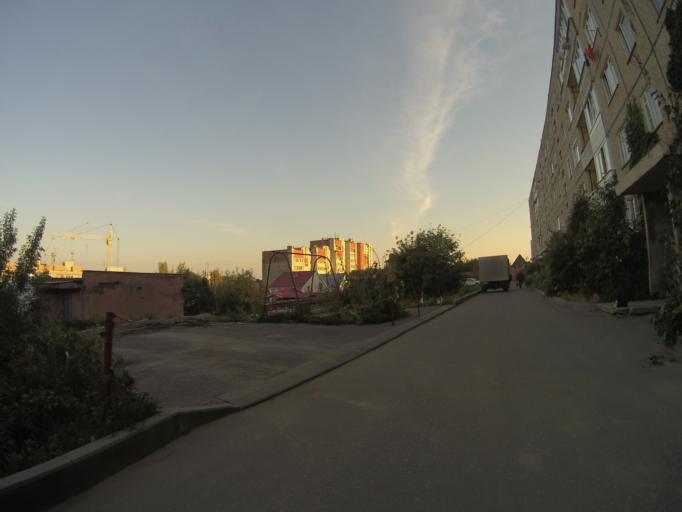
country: RU
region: Vladimir
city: Vladimir
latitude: 56.1135
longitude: 40.3768
